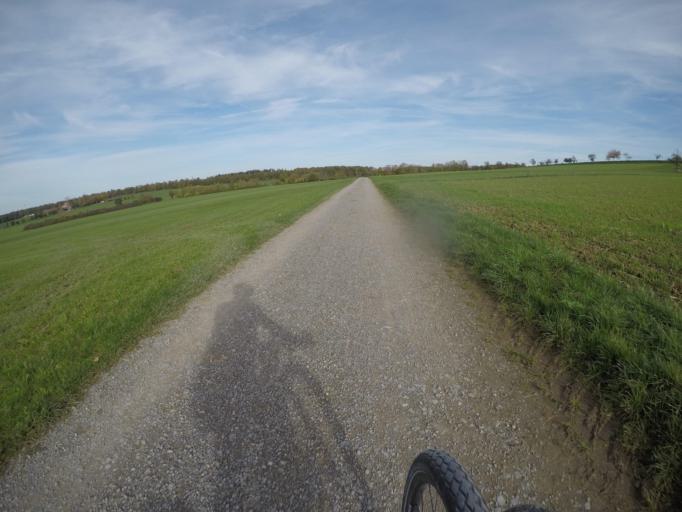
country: DE
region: Baden-Wuerttemberg
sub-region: Karlsruhe Region
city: Simmozheim
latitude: 48.7509
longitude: 8.7844
